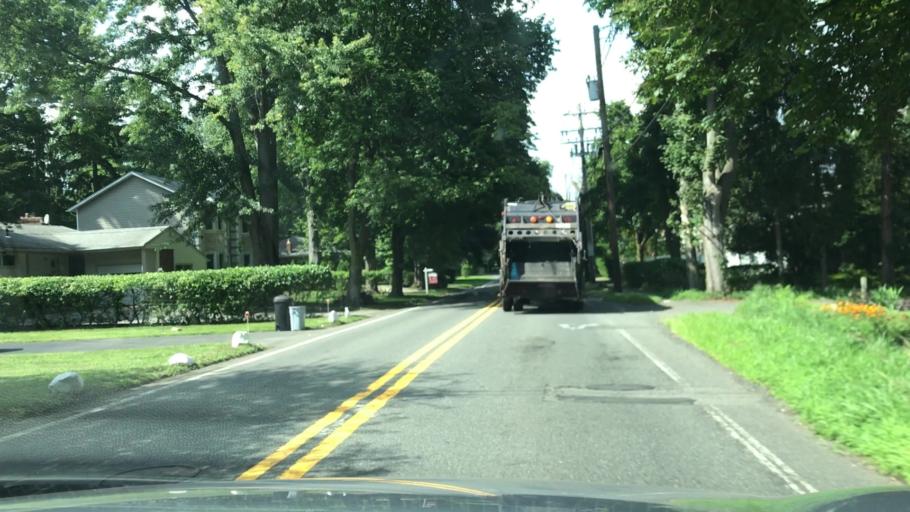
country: US
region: New Jersey
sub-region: Bergen County
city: Demarest
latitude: 40.9591
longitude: -73.9749
